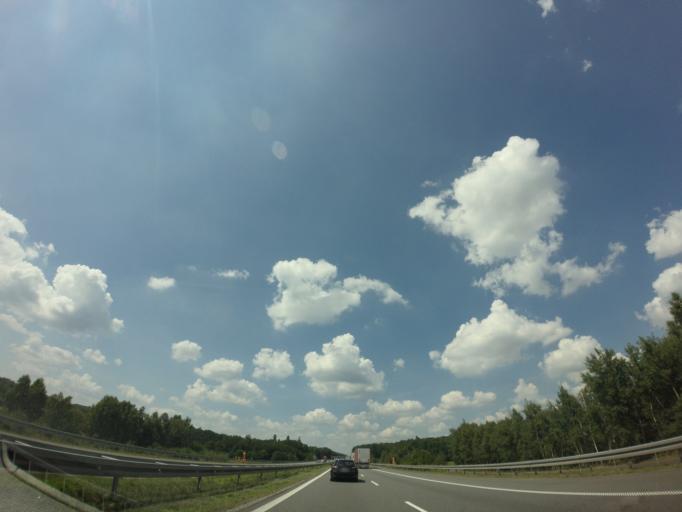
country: PL
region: Opole Voivodeship
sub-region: Powiat opolski
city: Proszkow
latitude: 50.5805
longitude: 17.8343
